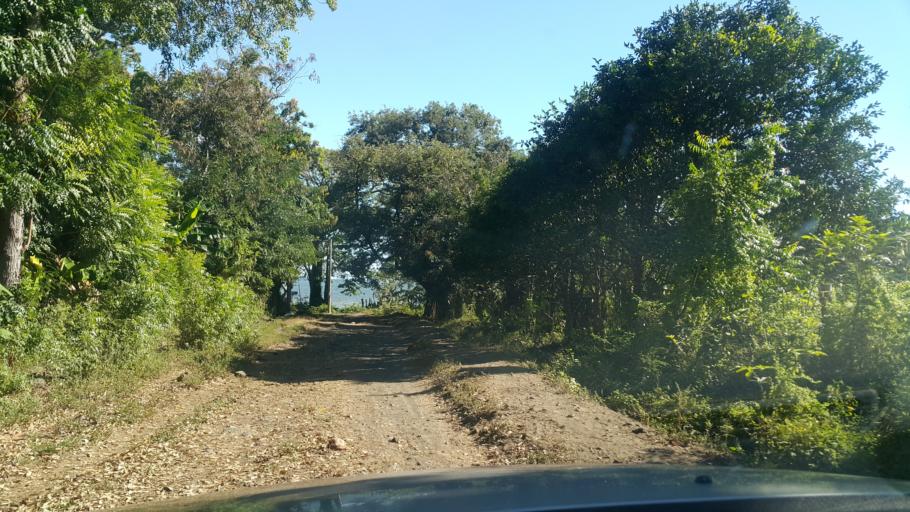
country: NI
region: Rivas
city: Altagracia
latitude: 11.4901
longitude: -85.5979
